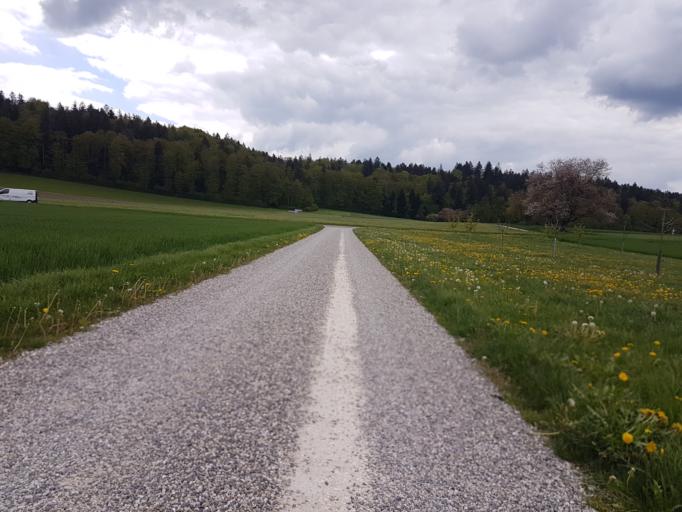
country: CH
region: Bern
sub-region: Oberaargau
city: Aarwangen
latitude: 47.2362
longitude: 7.7536
